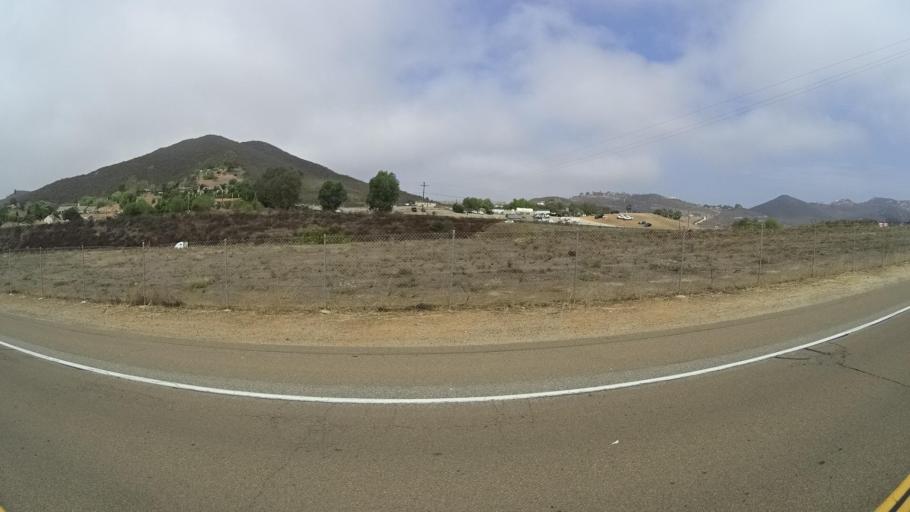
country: US
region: California
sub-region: San Diego County
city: Rainbow
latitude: 33.4005
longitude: -117.1689
